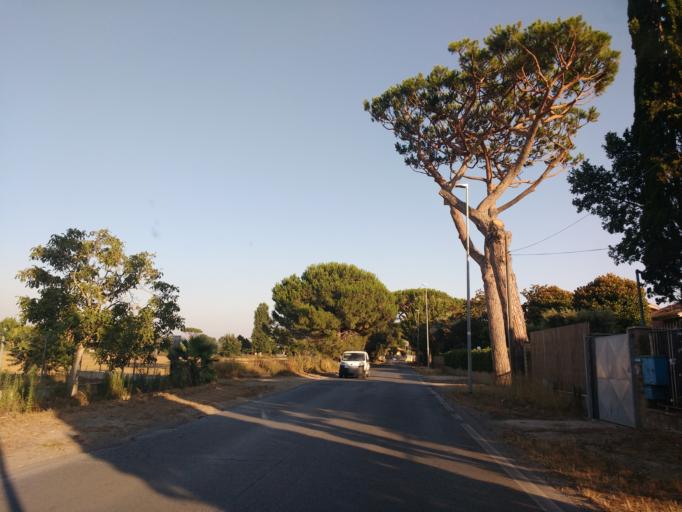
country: IT
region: Latium
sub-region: Citta metropolitana di Roma Capitale
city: Fregene
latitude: 41.8558
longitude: 12.2170
